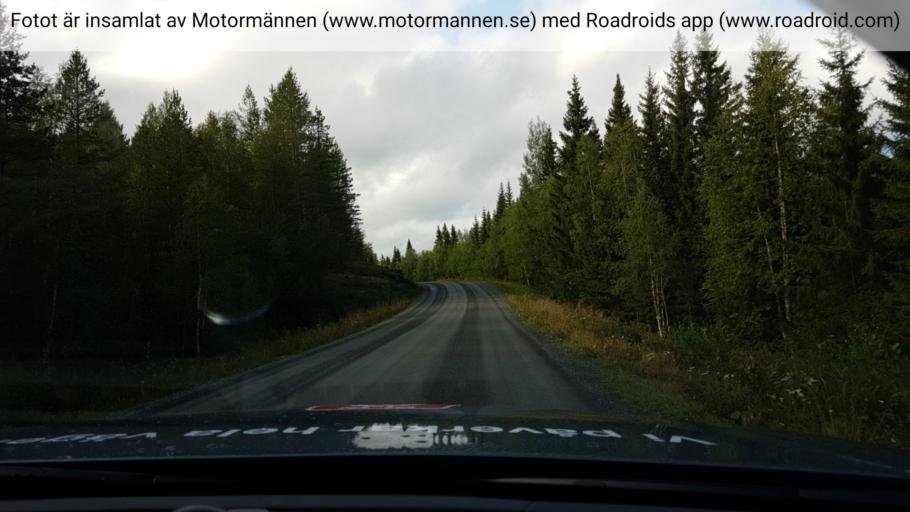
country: SE
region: Jaemtland
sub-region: Krokoms Kommun
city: Krokom
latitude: 63.7297
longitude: 14.5039
